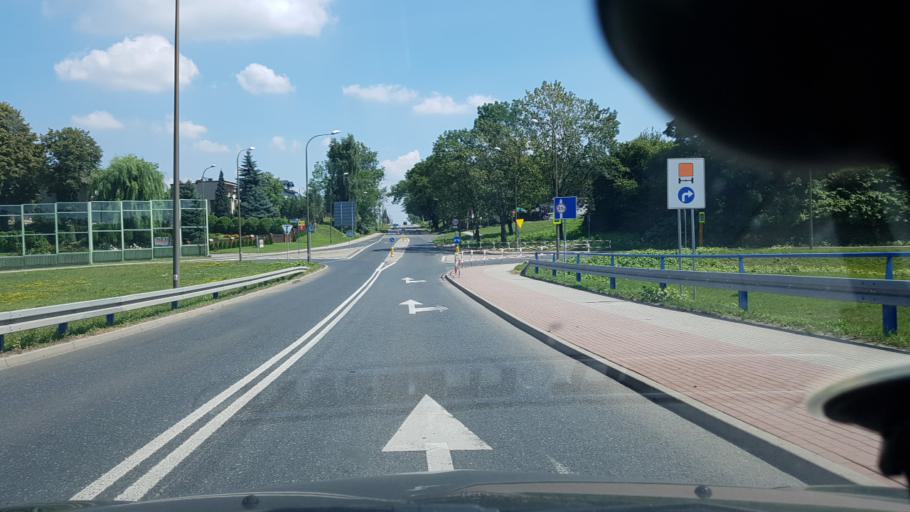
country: PL
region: Silesian Voivodeship
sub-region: Zory
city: Zory
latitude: 50.0399
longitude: 18.6741
